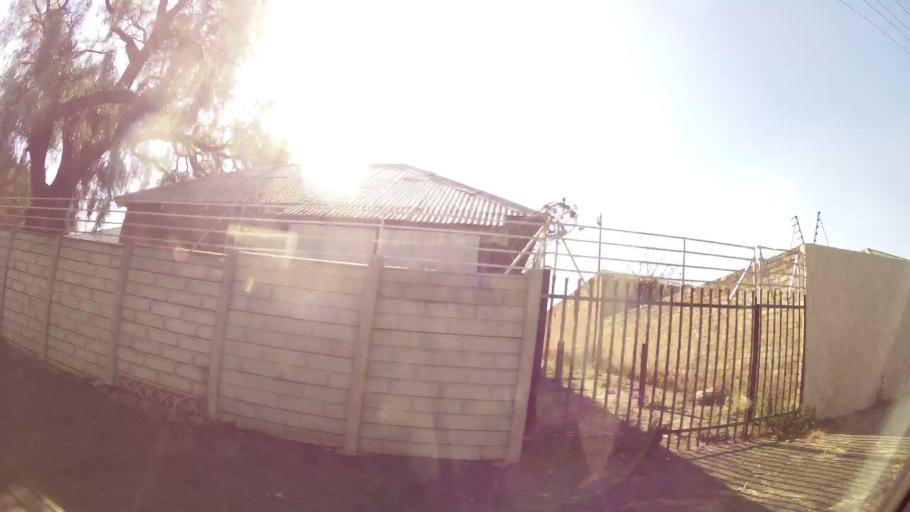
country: ZA
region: Gauteng
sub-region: City of Johannesburg Metropolitan Municipality
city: Johannesburg
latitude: -26.2604
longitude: 28.0516
